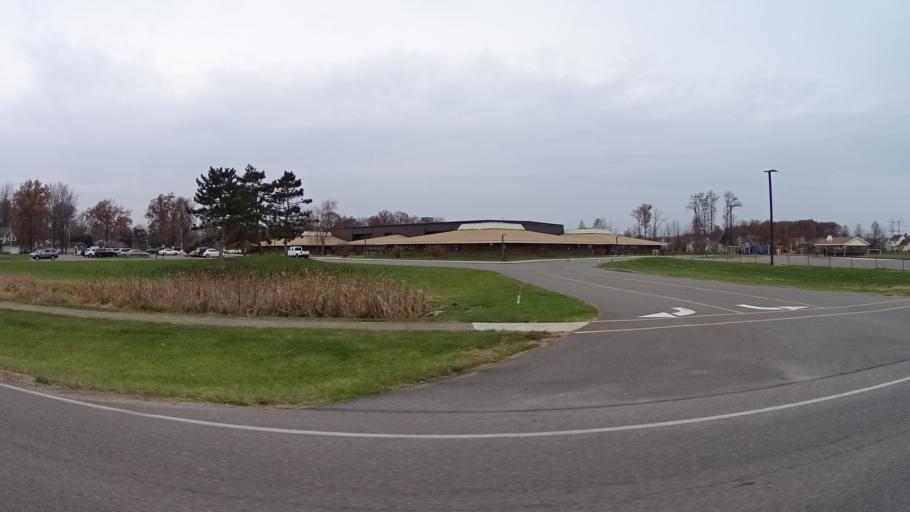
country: US
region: Ohio
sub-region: Lorain County
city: North Ridgeville
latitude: 41.4063
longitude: -82.0064
